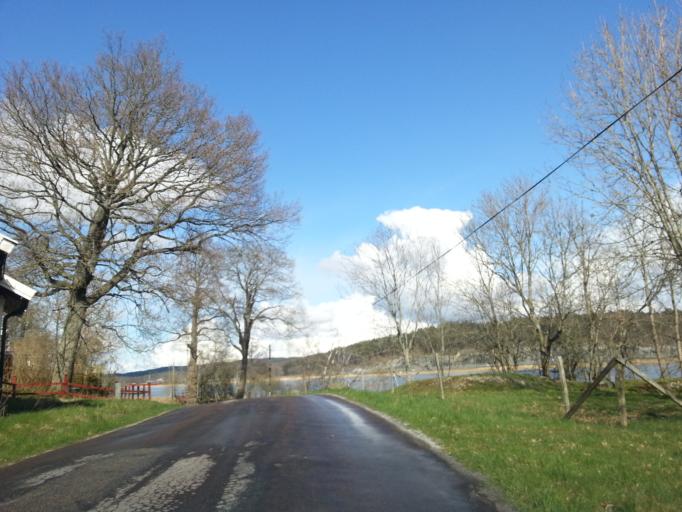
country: SE
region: Vaestra Goetaland
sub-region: Kungalvs Kommun
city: Diserod
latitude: 57.8821
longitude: 12.0265
